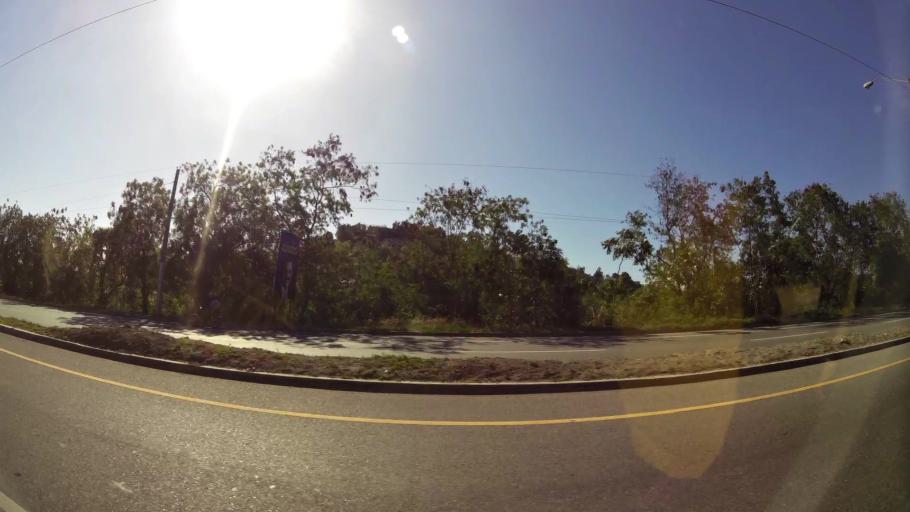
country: DO
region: San Cristobal
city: El Carril
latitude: 18.4409
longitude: -70.0039
